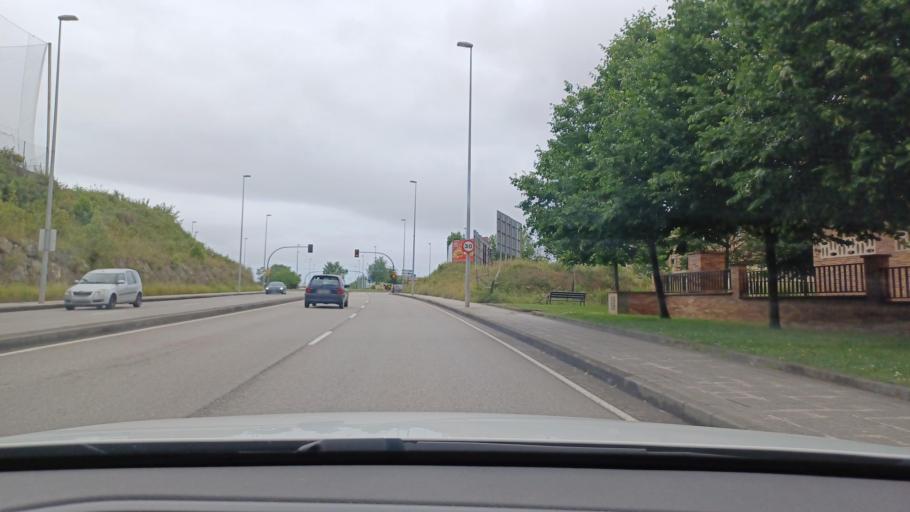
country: ES
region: Asturias
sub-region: Province of Asturias
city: Gijon
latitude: 43.5259
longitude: -5.6553
